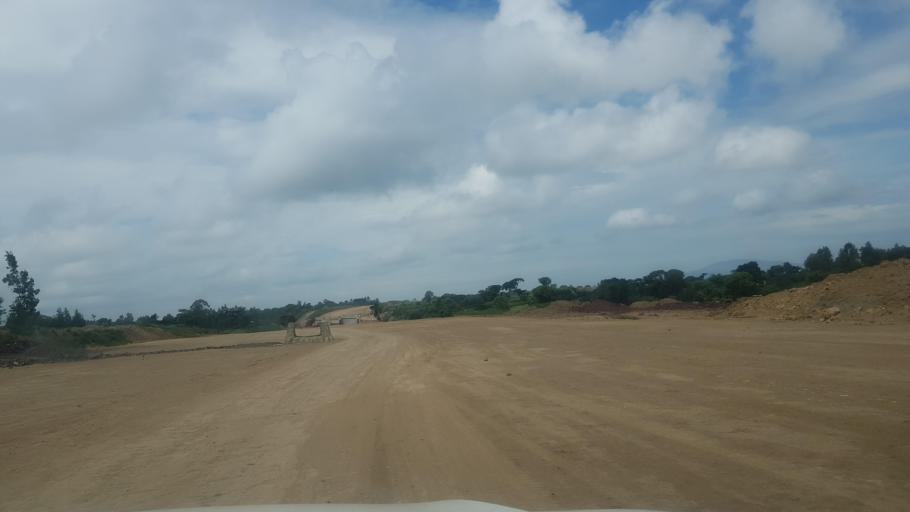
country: ET
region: Oromiya
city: Shashemene
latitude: 7.2527
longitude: 38.5922
